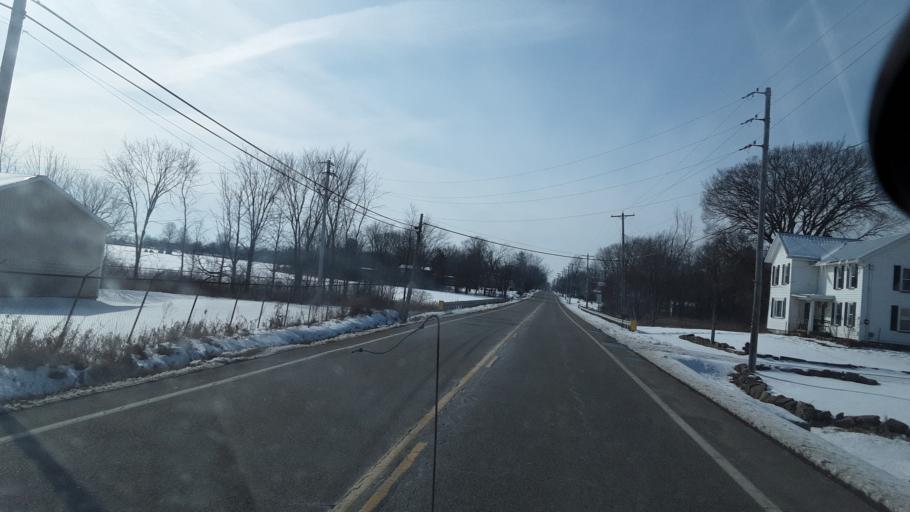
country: US
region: Ohio
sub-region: Mahoning County
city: Sebring
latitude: 41.0247
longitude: -81.0371
